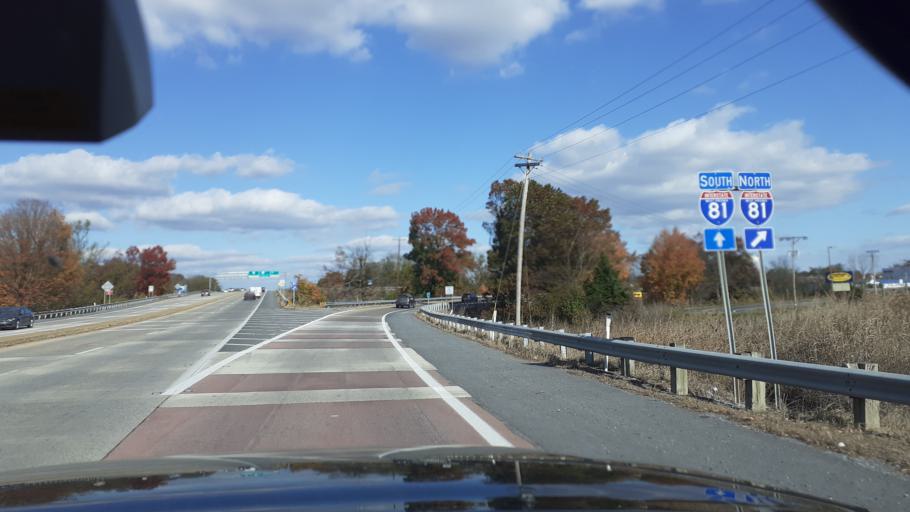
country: US
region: West Virginia
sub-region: Berkeley County
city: Martinsburg
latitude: 39.4927
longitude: -77.9587
